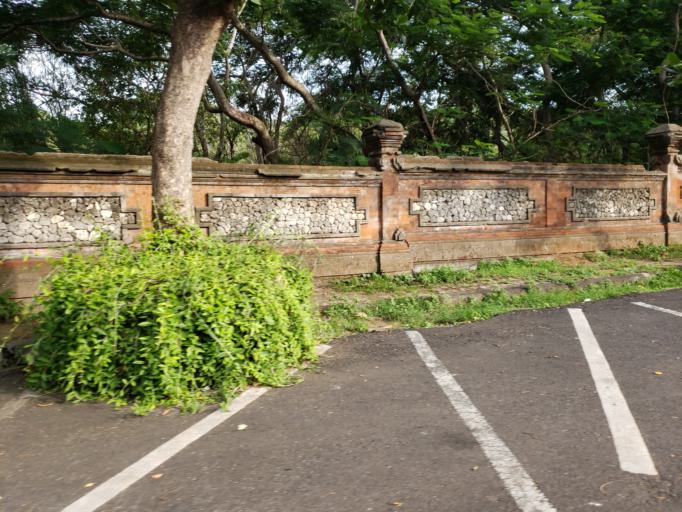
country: ID
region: Bali
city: Pecatu
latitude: -8.8289
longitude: 115.0870
